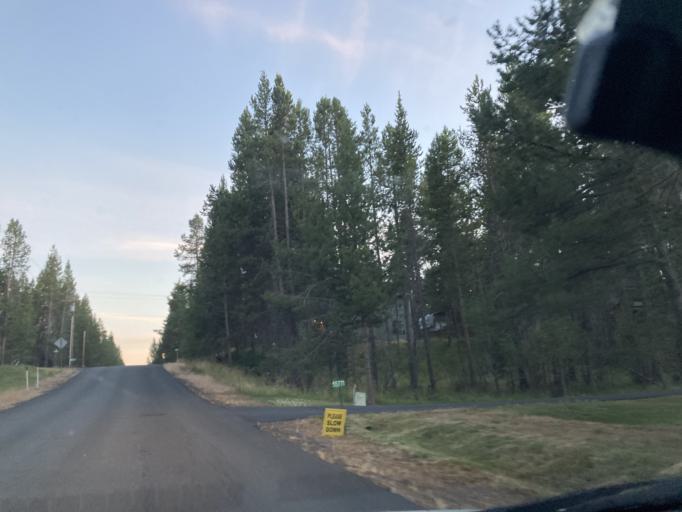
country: US
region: Oregon
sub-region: Deschutes County
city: Three Rivers
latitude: 43.8260
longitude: -121.4656
